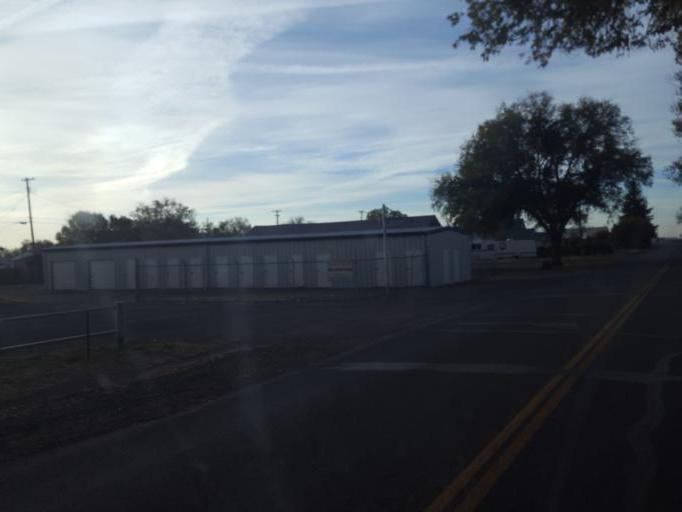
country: US
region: Colorado
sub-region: Saguache County
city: Center
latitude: 37.7512
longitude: -106.1084
